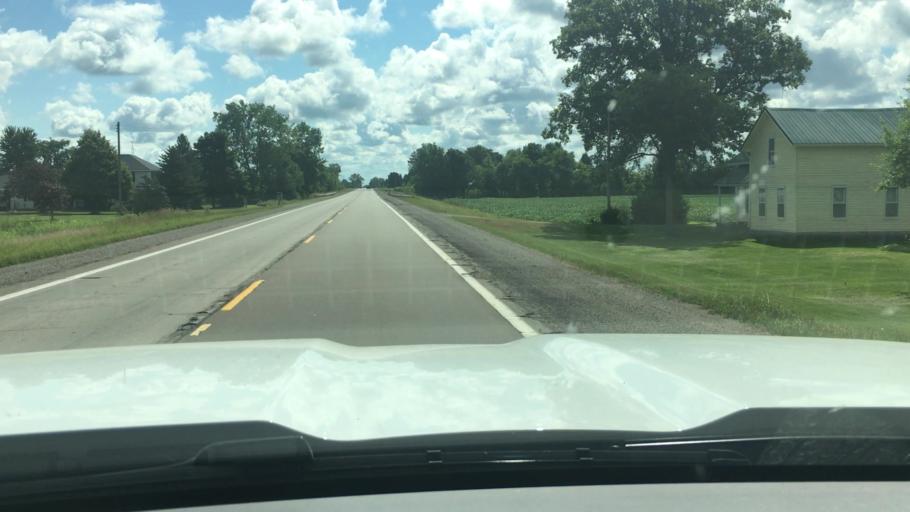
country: US
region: Michigan
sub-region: Shiawassee County
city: New Haven
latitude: 43.1870
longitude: -84.2551
